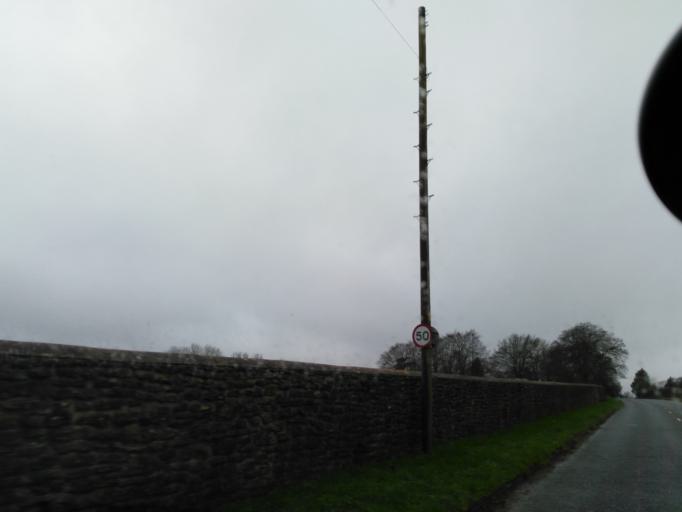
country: GB
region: England
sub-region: Wiltshire
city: Westwood
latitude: 51.3486
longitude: -2.2692
